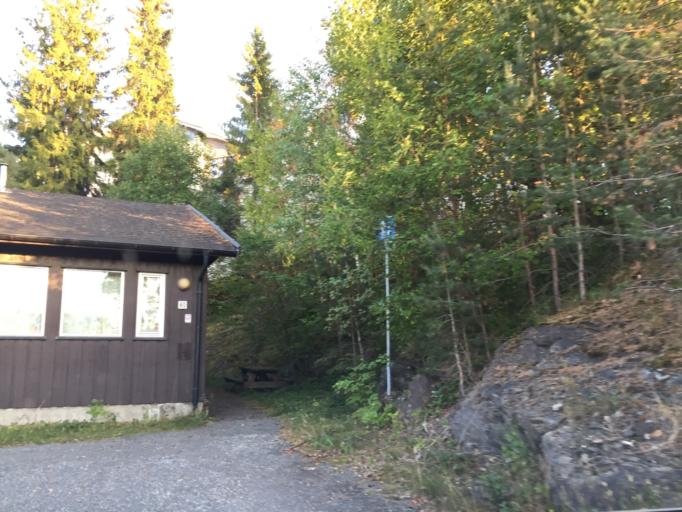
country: NO
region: Akershus
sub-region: Baerum
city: Lysaker
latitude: 59.8892
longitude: 10.6224
